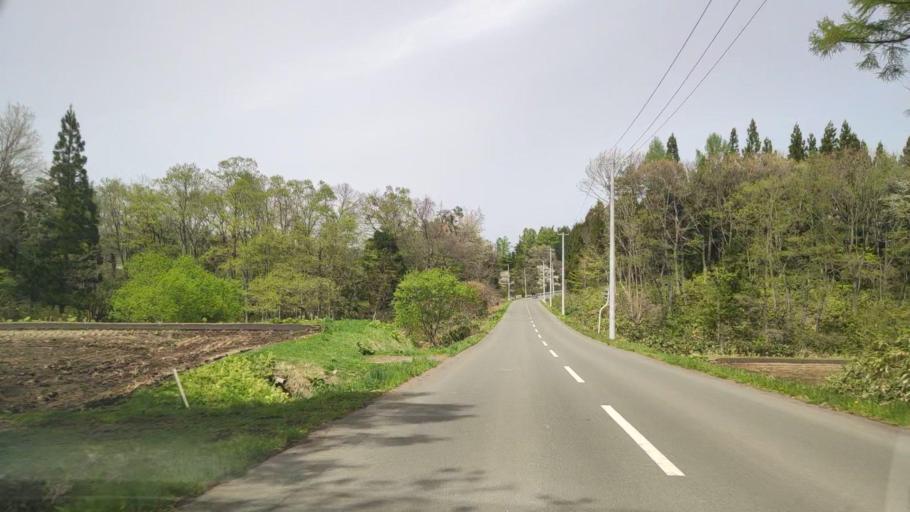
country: JP
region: Aomori
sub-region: Misawa Shi
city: Inuotose
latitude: 40.7559
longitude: 141.1179
